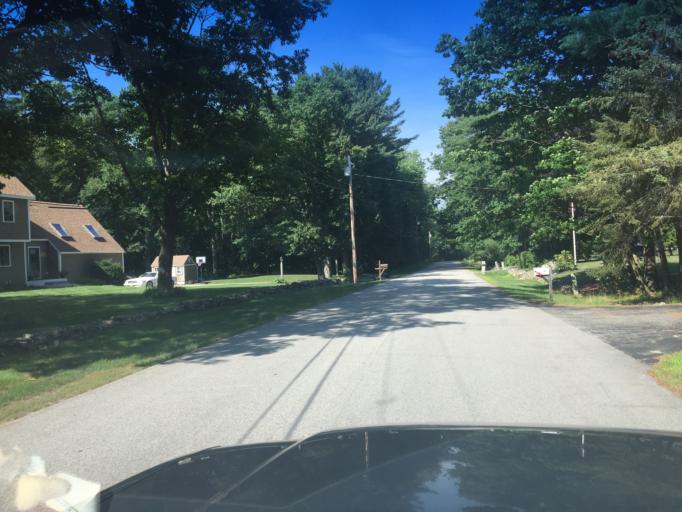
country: US
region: Maine
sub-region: York County
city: York Harbor
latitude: 43.1570
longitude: -70.6432
